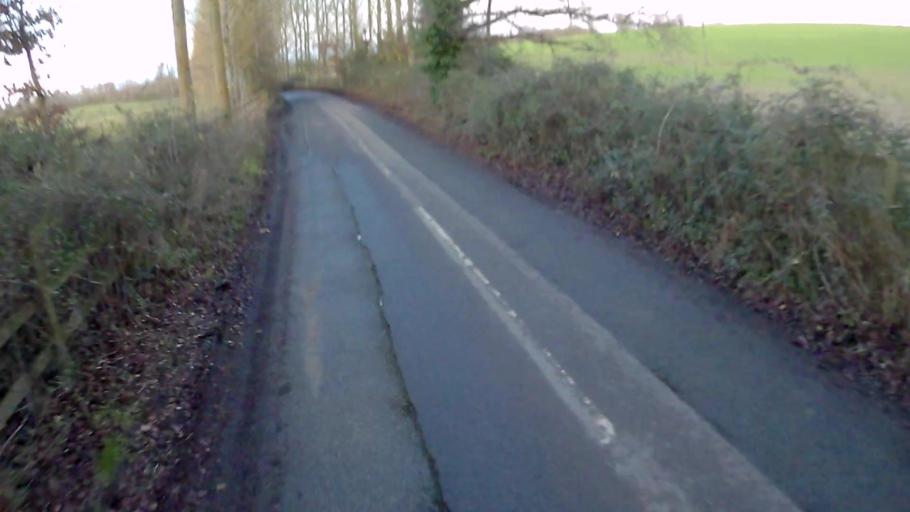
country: GB
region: England
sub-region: Hampshire
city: Overton
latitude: 51.2405
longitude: -1.2179
